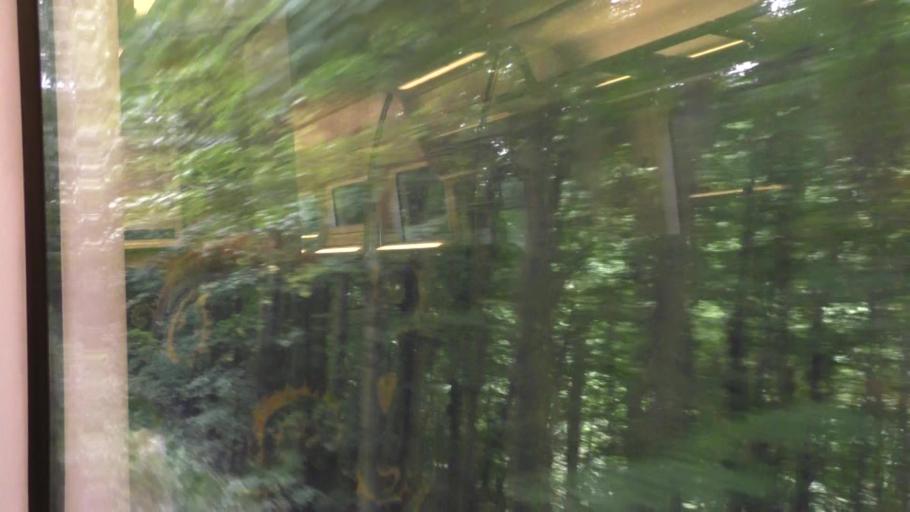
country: DE
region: Saxony
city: Schlegel
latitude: 50.9688
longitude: 14.9048
